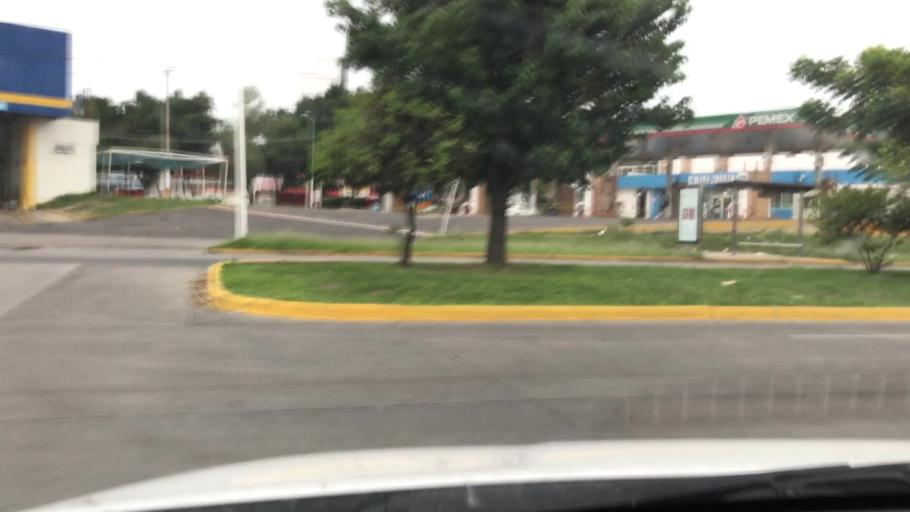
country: MX
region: Jalisco
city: Guadalajara
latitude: 20.6593
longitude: -103.4226
